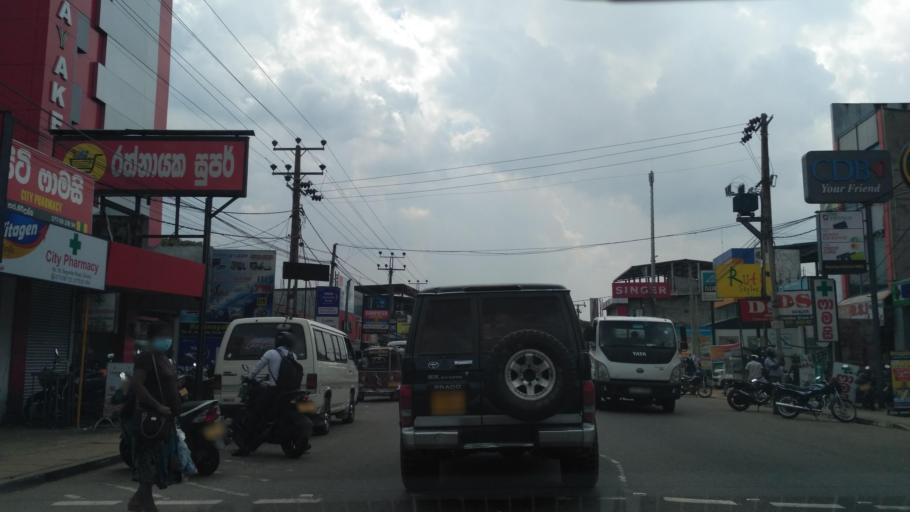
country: LK
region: North Western
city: Kuliyapitiya
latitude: 7.3289
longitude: 80.1217
